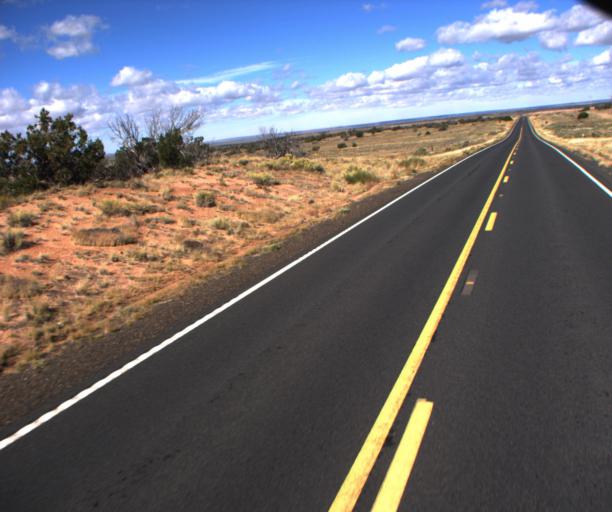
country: US
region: Arizona
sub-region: Apache County
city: Houck
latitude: 35.0776
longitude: -109.2985
